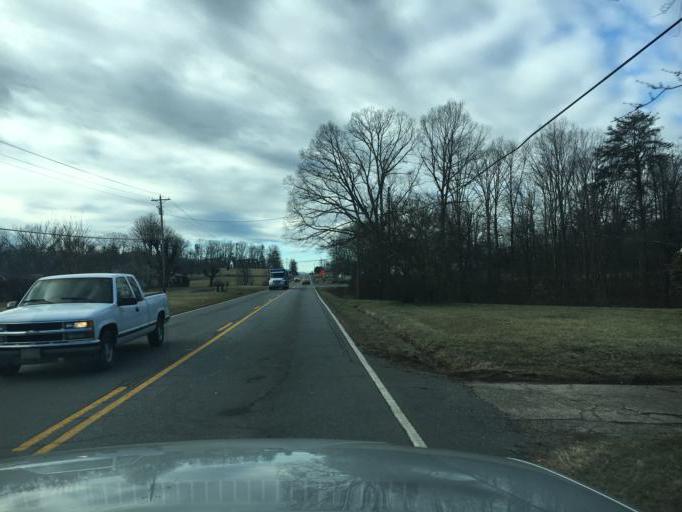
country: US
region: North Carolina
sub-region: Burke County
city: Salem
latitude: 35.6851
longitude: -81.7277
